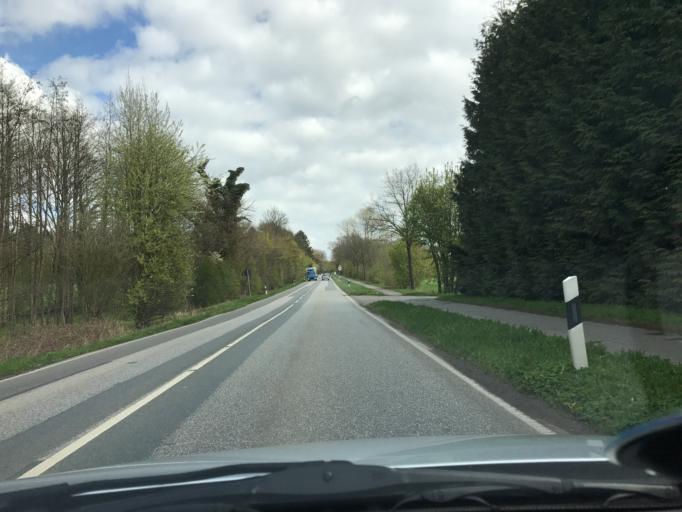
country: DE
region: Schleswig-Holstein
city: Susel
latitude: 54.0879
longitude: 10.7315
